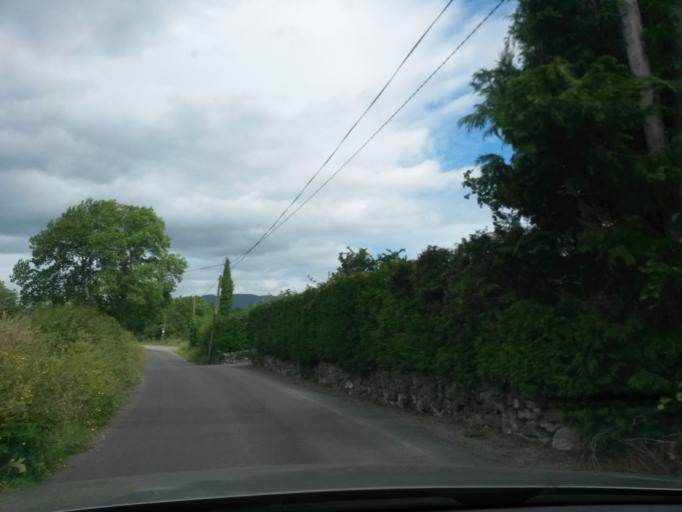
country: IE
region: Connaught
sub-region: County Leitrim
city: Manorhamilton
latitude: 54.2298
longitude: -8.3125
